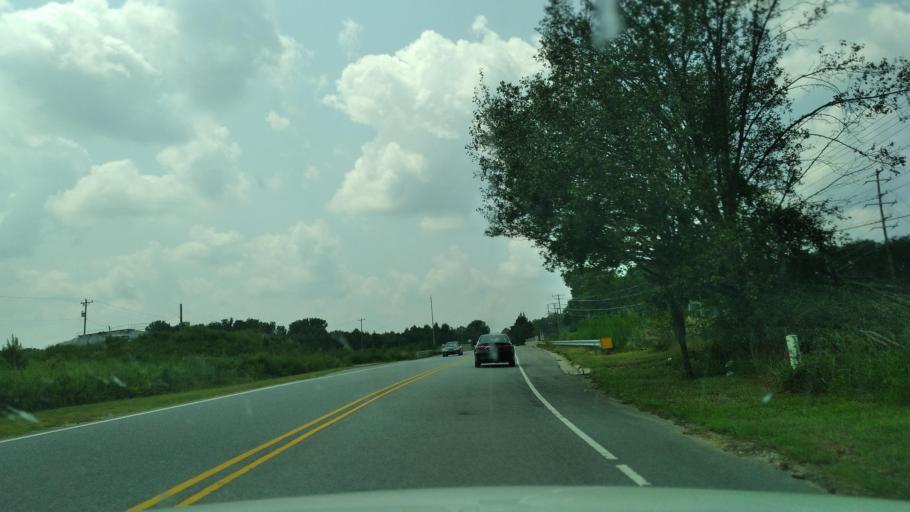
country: US
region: North Carolina
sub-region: Guilford County
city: Summerfield
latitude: 36.1243
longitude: -79.9008
